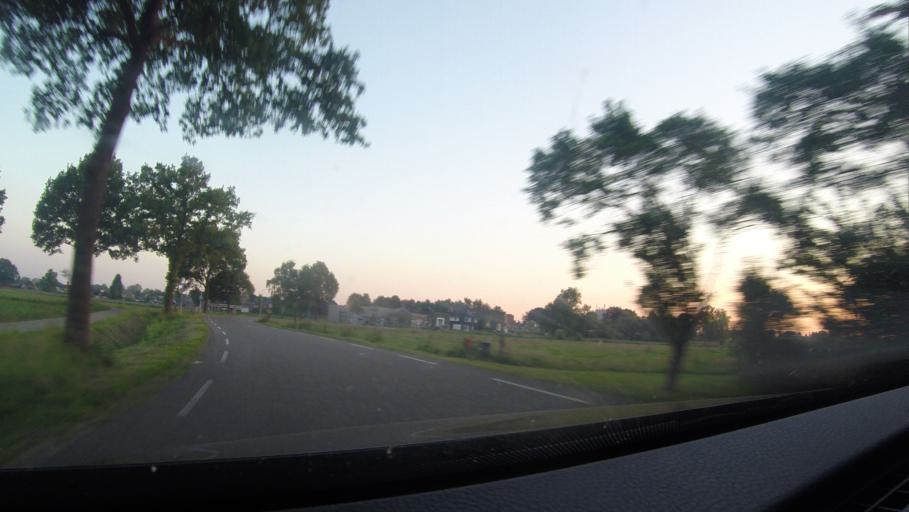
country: NL
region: Overijssel
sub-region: Gemeente Raalte
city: Raalte
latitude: 52.3253
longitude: 6.2830
